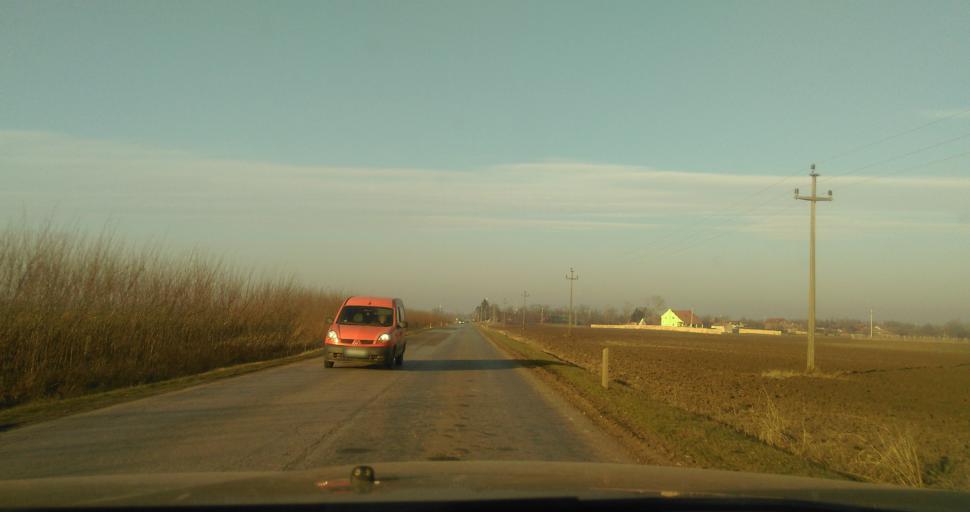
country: RS
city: Backo Gradiste
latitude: 45.5137
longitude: 20.0265
